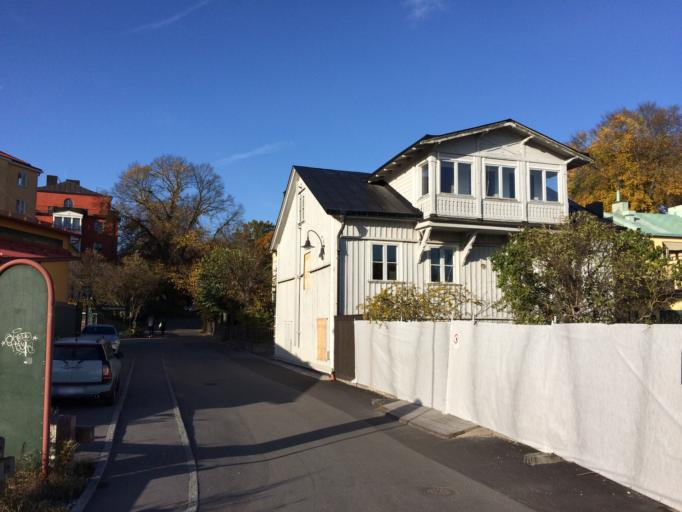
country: SE
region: Stockholm
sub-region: Stockholms Kommun
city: OEstermalm
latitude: 59.3222
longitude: 18.1021
